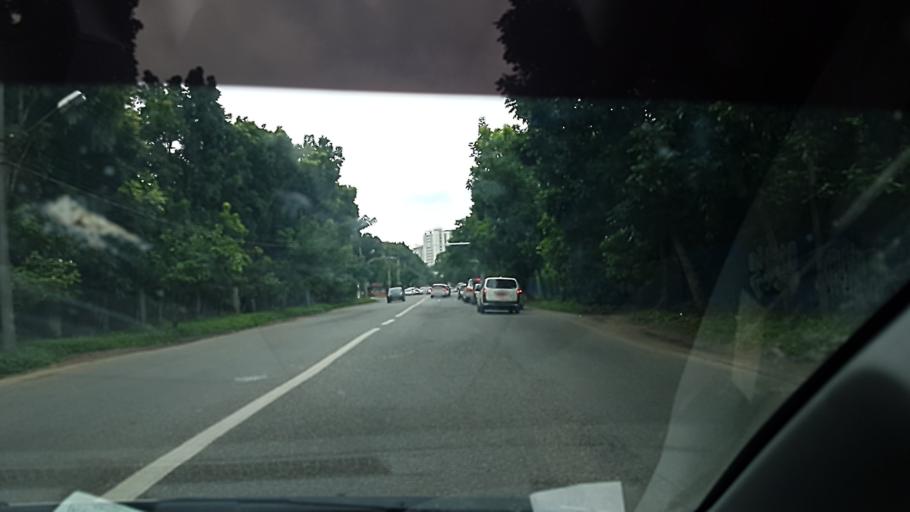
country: MM
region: Yangon
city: Yangon
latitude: 16.7918
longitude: 96.1328
